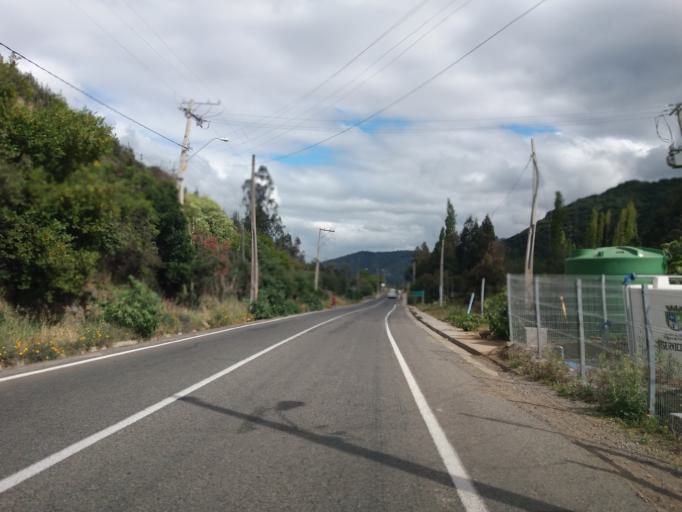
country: CL
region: Valparaiso
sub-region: Provincia de Marga Marga
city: Limache
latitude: -33.0605
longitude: -71.0788
